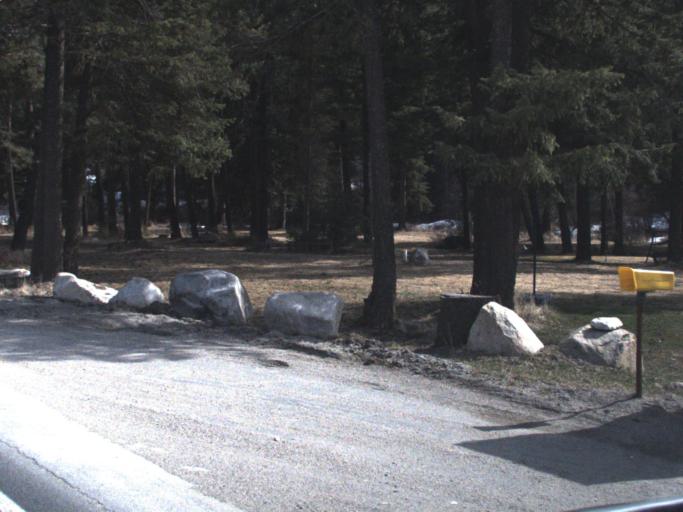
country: US
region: Washington
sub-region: Stevens County
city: Chewelah
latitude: 48.5256
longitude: -117.6394
